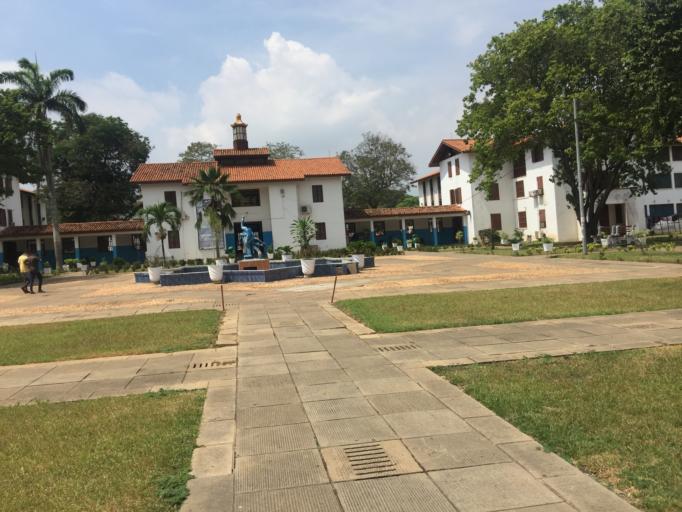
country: GH
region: Greater Accra
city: Medina Estates
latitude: 5.6457
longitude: -0.1871
